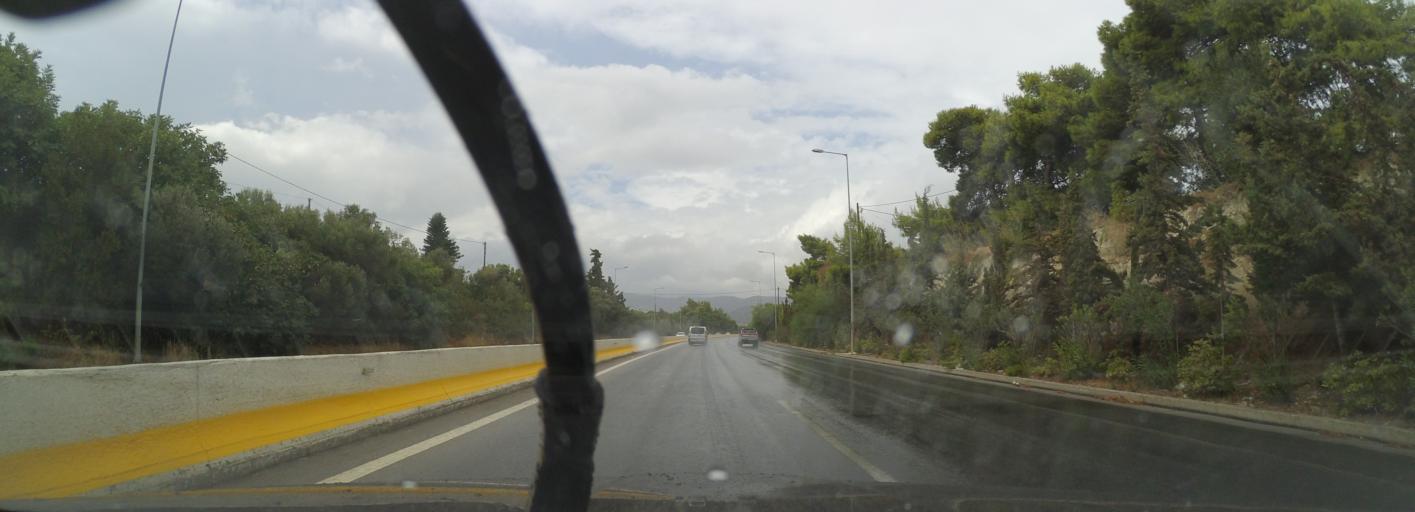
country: GR
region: Crete
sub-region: Nomos Irakleiou
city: Gazi
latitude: 35.3172
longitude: 25.0775
